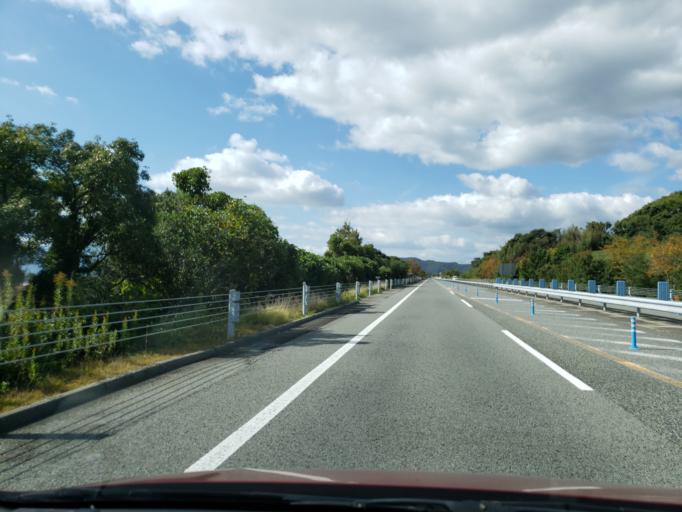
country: JP
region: Tokushima
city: Kamojimacho-jogejima
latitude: 34.1199
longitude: 134.3488
